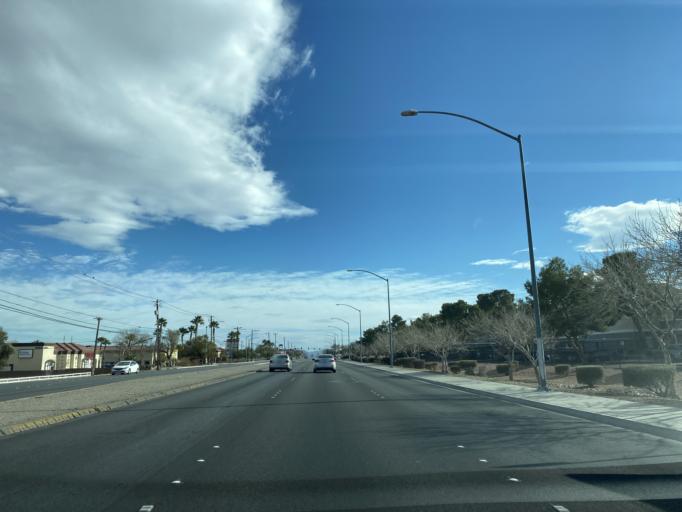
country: US
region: Nevada
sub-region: Clark County
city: Las Vegas
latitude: 36.2271
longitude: -115.2213
